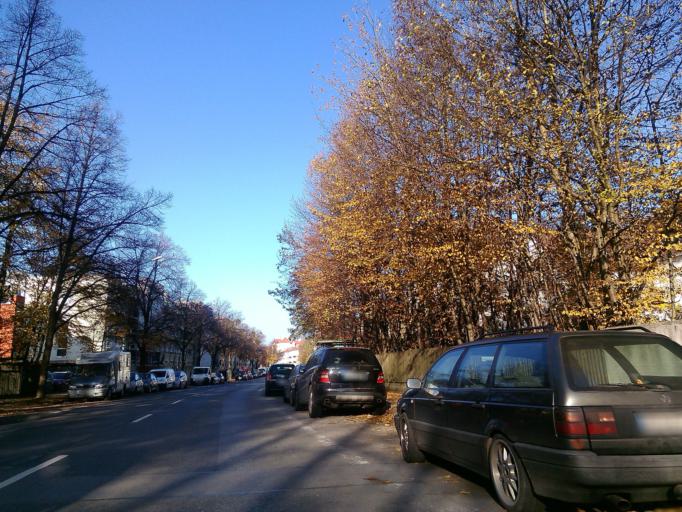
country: DE
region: Bavaria
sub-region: Upper Bavaria
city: Pasing
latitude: 48.1342
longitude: 11.4519
